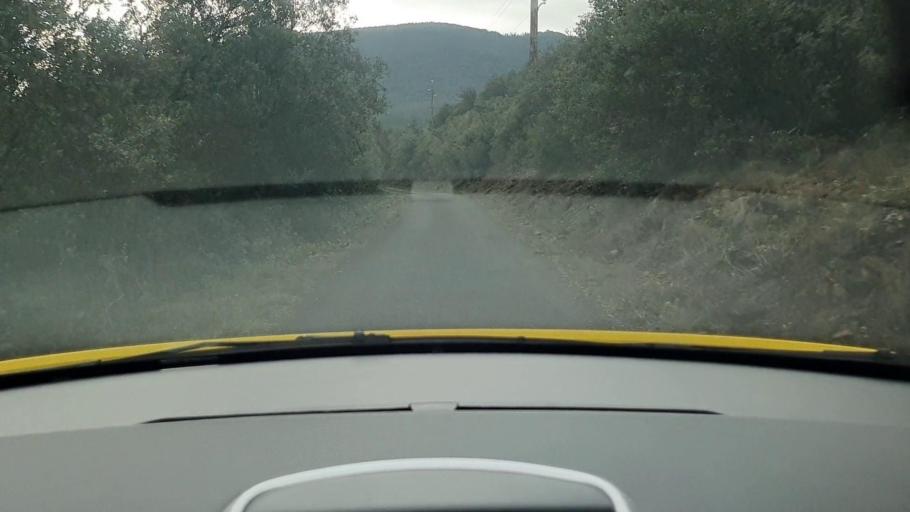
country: FR
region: Languedoc-Roussillon
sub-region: Departement du Gard
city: Saint-Florent-sur-Auzonnet
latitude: 44.2640
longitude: 4.1240
